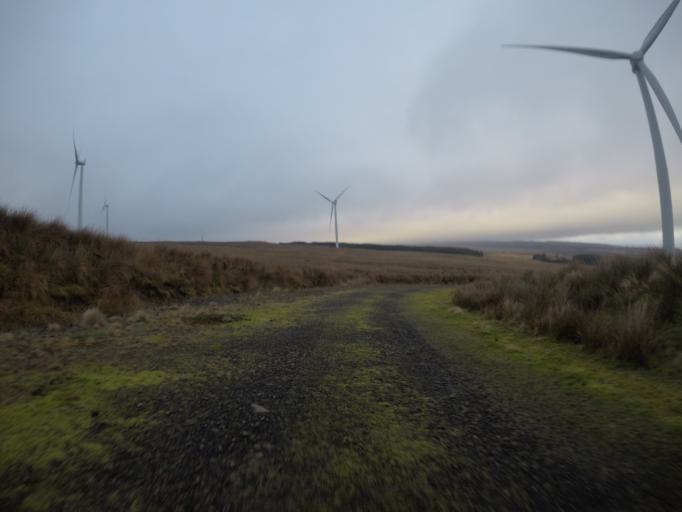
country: GB
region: Scotland
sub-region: North Ayrshire
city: Dalry
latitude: 55.7388
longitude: -4.7733
